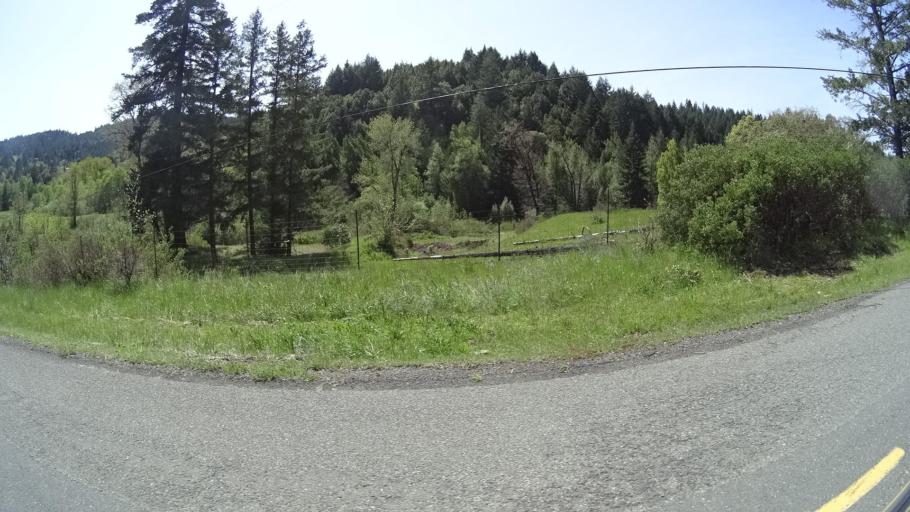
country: US
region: California
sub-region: Humboldt County
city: Redway
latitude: 40.3039
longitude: -123.6543
